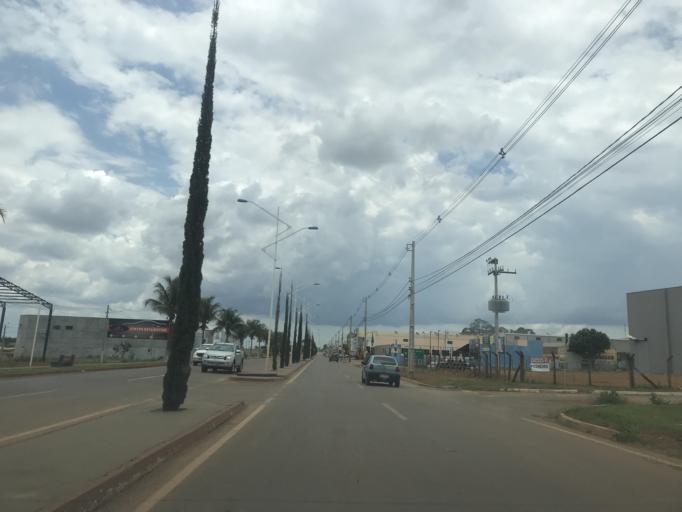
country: BR
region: Goias
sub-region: Vianopolis
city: Vianopolis
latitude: -16.7551
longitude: -48.5198
